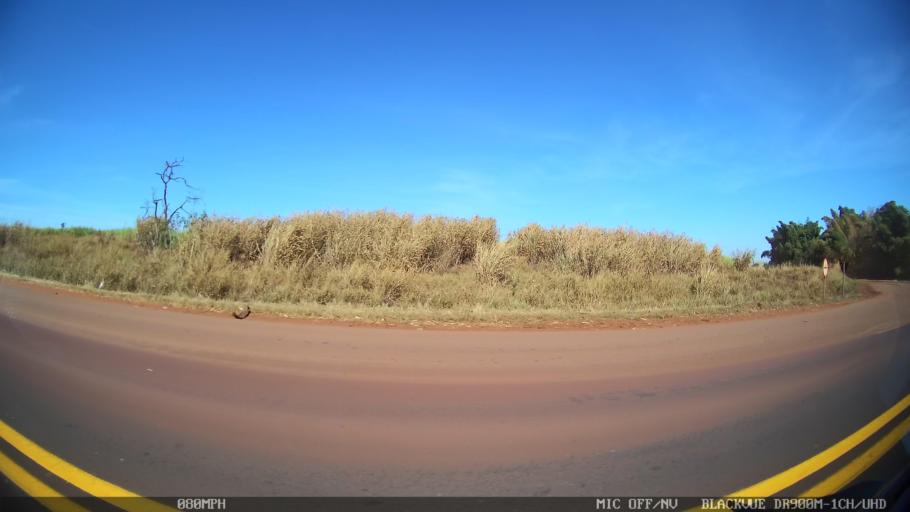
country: BR
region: Sao Paulo
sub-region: Barretos
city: Barretos
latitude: -20.4662
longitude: -48.4769
